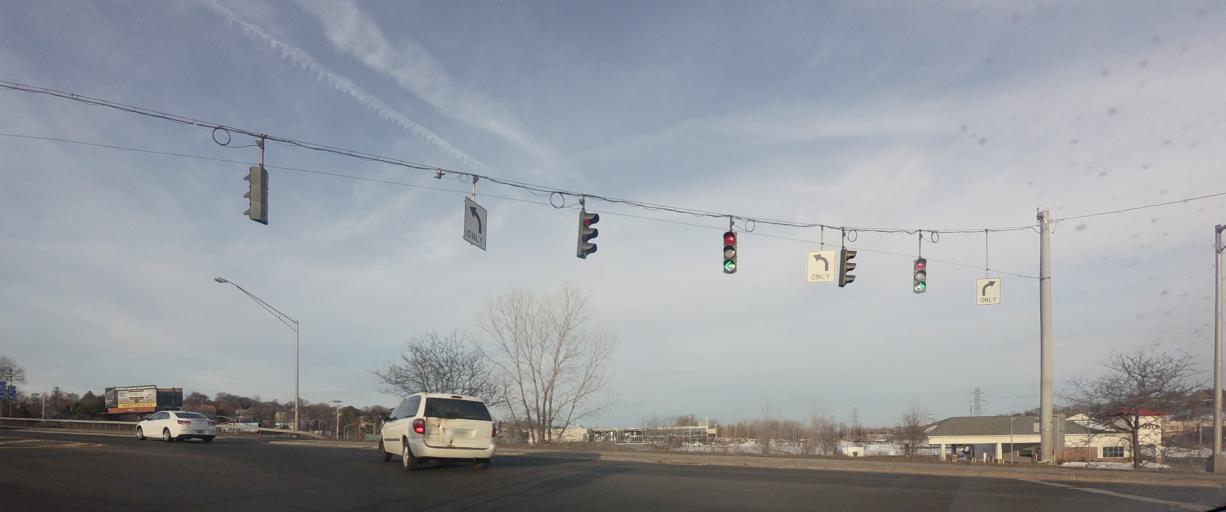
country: US
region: New York
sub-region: Onondaga County
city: East Syracuse
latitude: 43.0565
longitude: -76.1041
